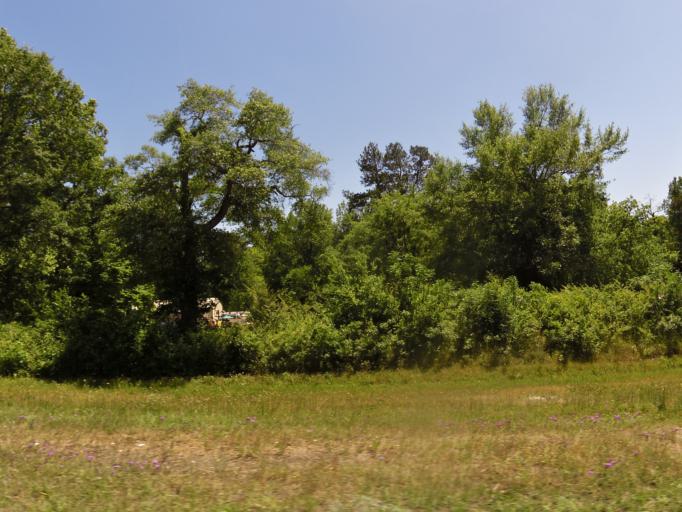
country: US
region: South Carolina
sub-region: Aiken County
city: Warrenville
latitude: 33.5539
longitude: -81.8122
